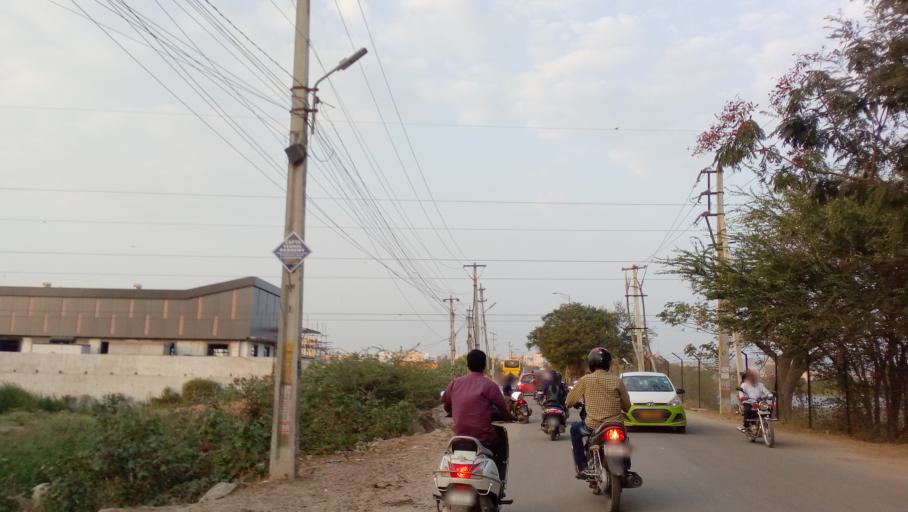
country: IN
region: Telangana
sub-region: Medak
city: Serilingampalle
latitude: 17.5128
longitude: 78.3184
